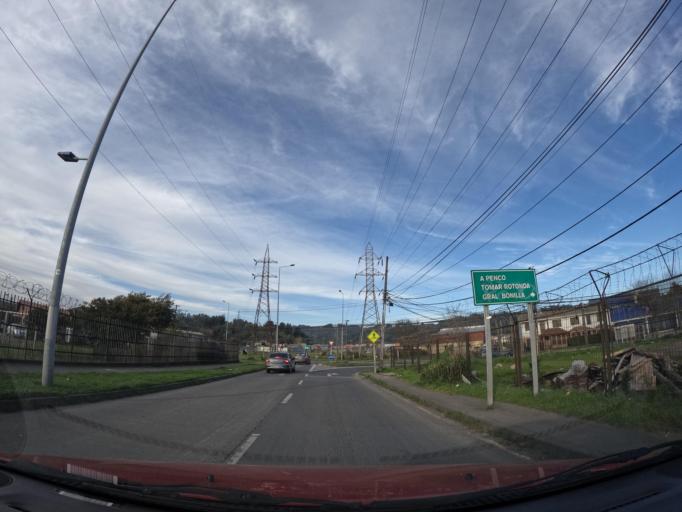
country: CL
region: Biobio
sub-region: Provincia de Concepcion
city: Concepcion
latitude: -36.8031
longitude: -73.0306
